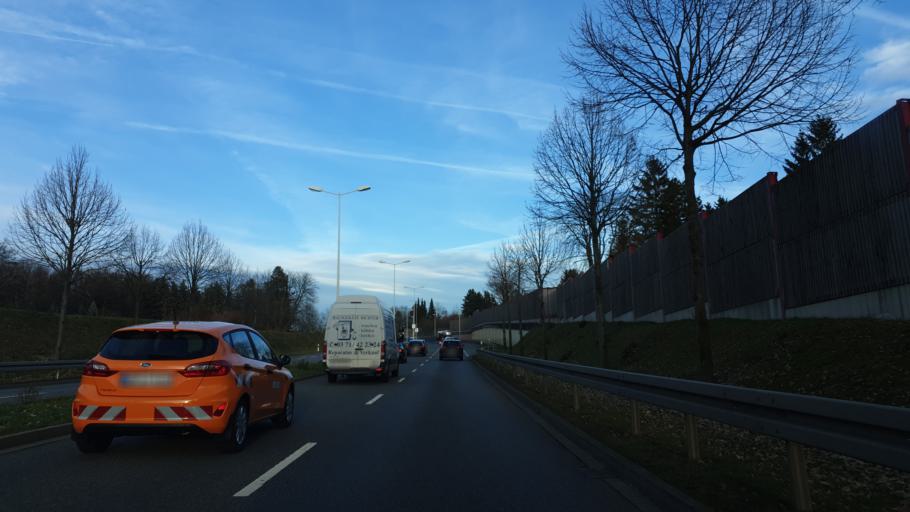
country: DE
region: Saxony
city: Chemnitz
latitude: 50.8093
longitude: 12.9571
